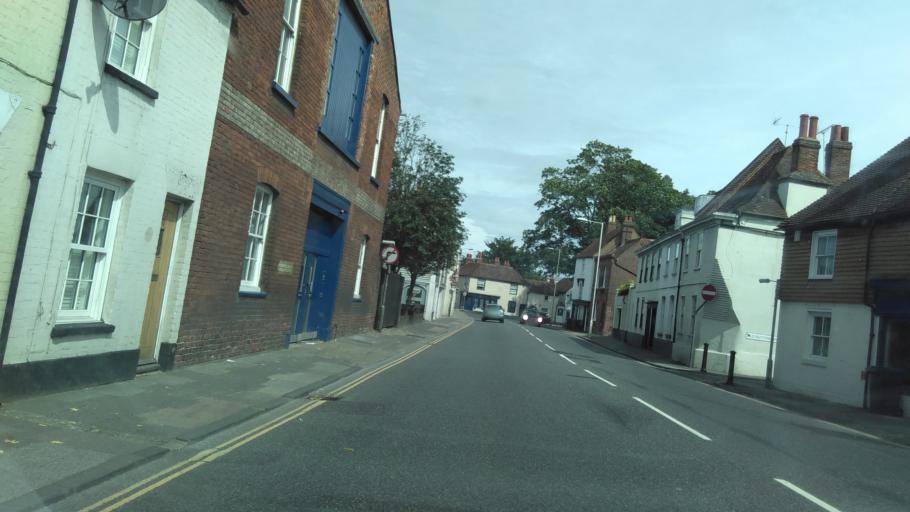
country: GB
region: England
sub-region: Kent
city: Canterbury
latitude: 51.2802
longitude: 1.0859
